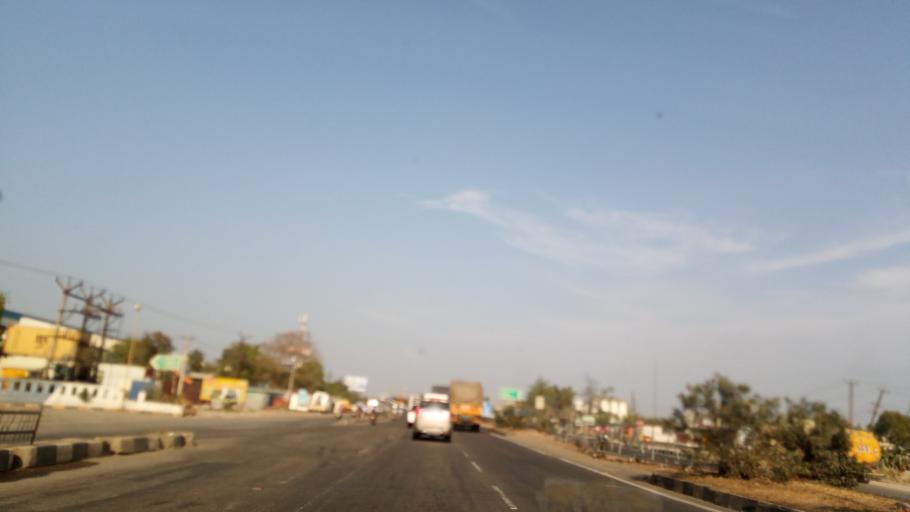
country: IN
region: Tamil Nadu
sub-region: Kancheepuram
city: Poonamalle
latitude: 13.0569
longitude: 80.1095
